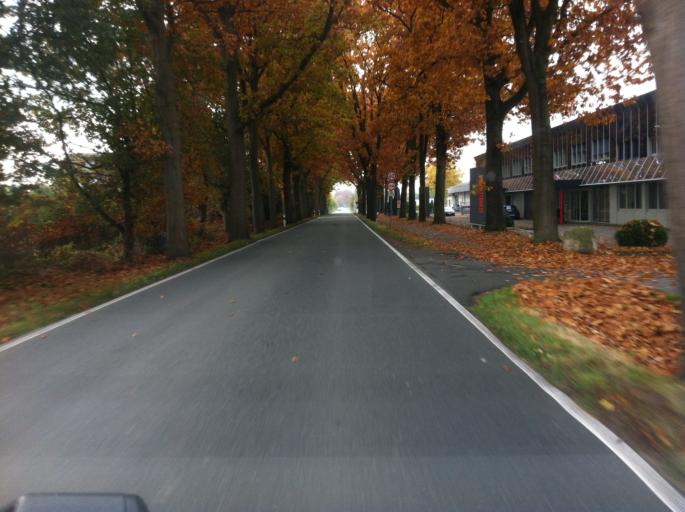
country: DE
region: North Rhine-Westphalia
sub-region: Regierungsbezirk Munster
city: Vreden
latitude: 52.0210
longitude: 6.8044
